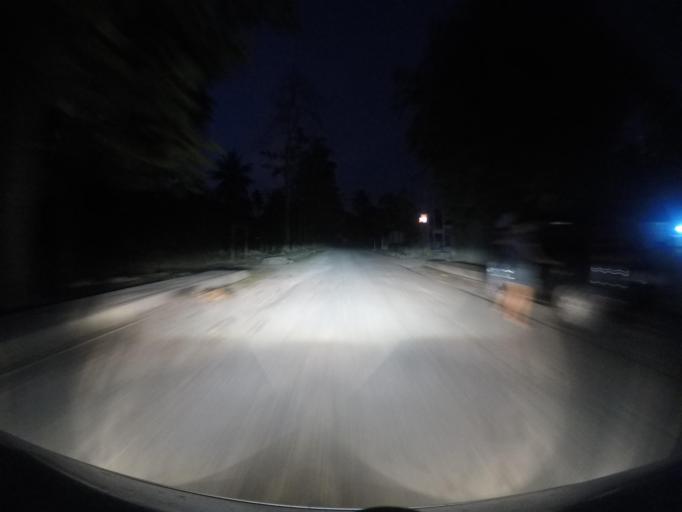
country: TL
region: Viqueque
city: Viqueque
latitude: -8.8508
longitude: 126.3660
